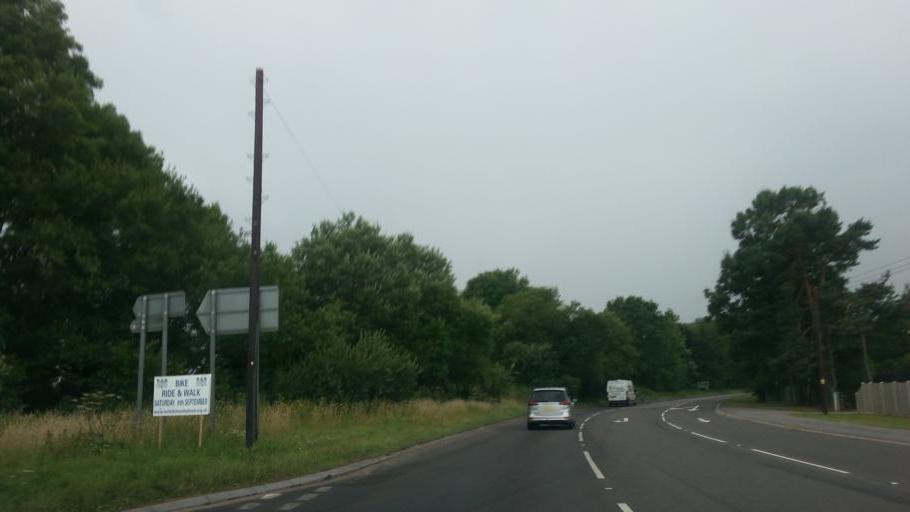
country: GB
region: England
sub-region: Norfolk
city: Briston
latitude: 52.8624
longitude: 0.9582
